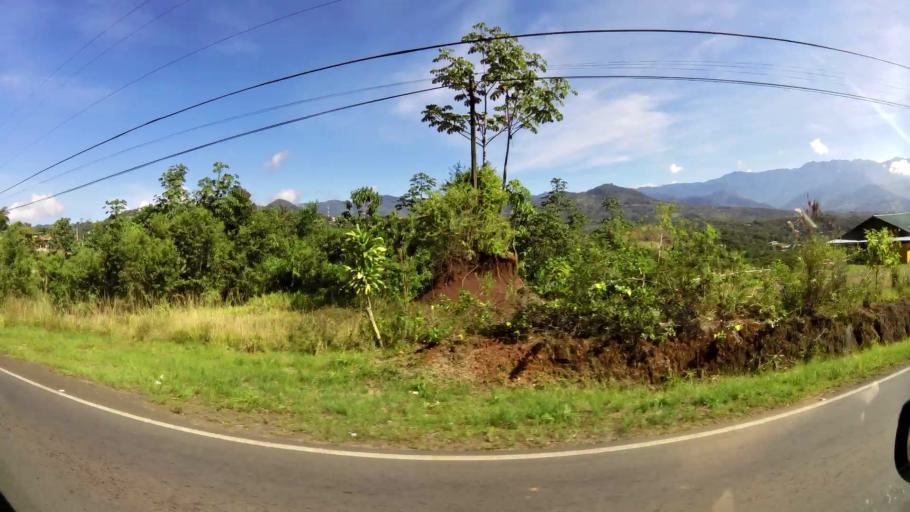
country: CR
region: San Jose
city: San Isidro
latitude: 9.3949
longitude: -83.7132
